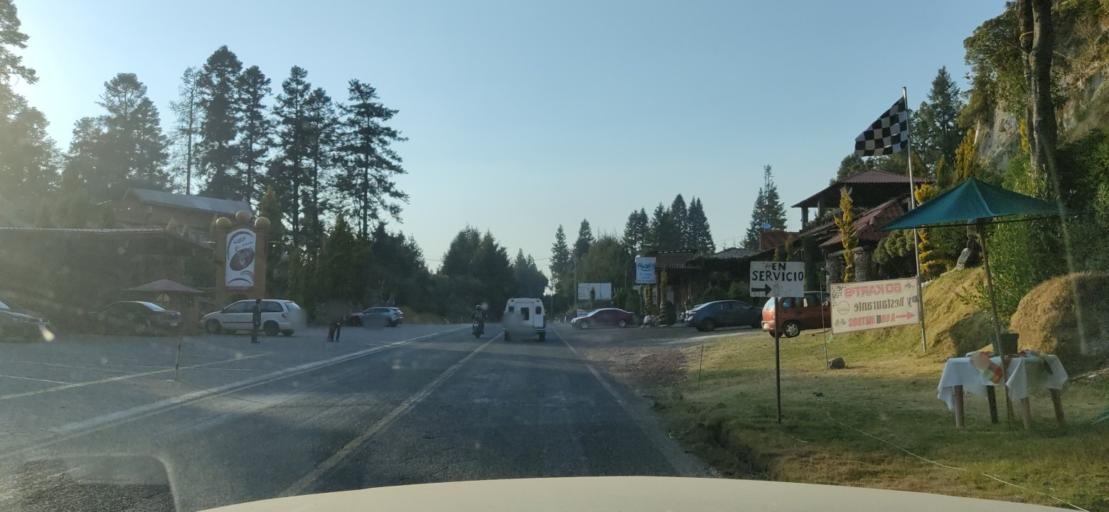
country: MX
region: Mexico
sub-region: Ocoyoacac
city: San Jeronimo Acazulco
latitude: 19.2517
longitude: -99.3747
